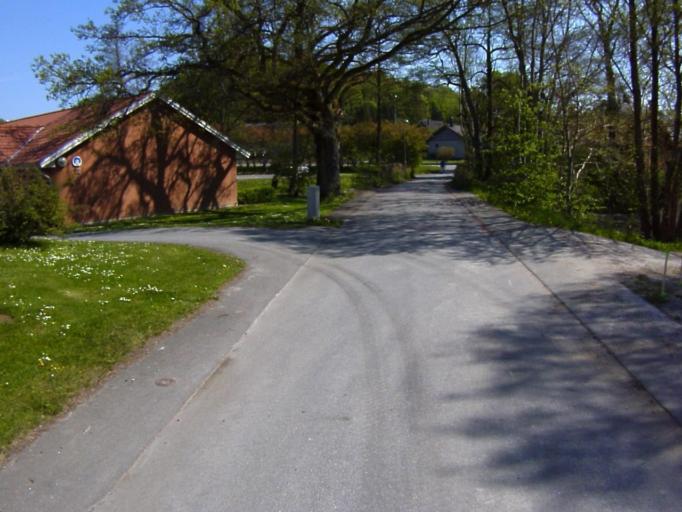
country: SE
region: Skane
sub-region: Kristianstads Kommun
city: Tollarp
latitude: 56.1749
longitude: 14.2883
